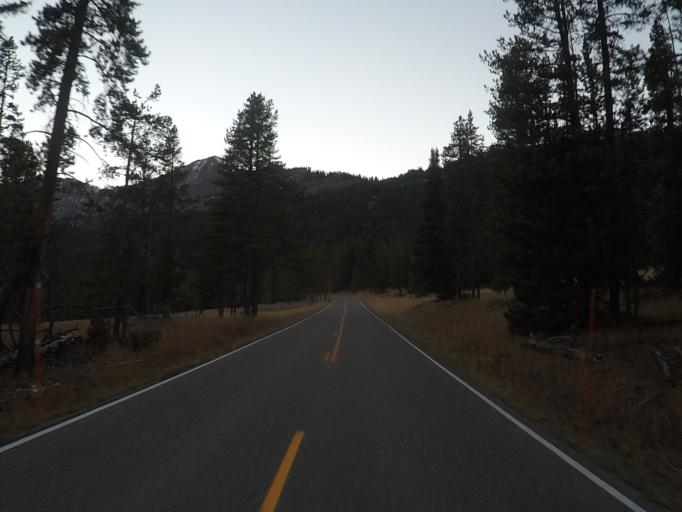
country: US
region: Montana
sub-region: Stillwater County
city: Absarokee
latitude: 45.0050
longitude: -110.0391
